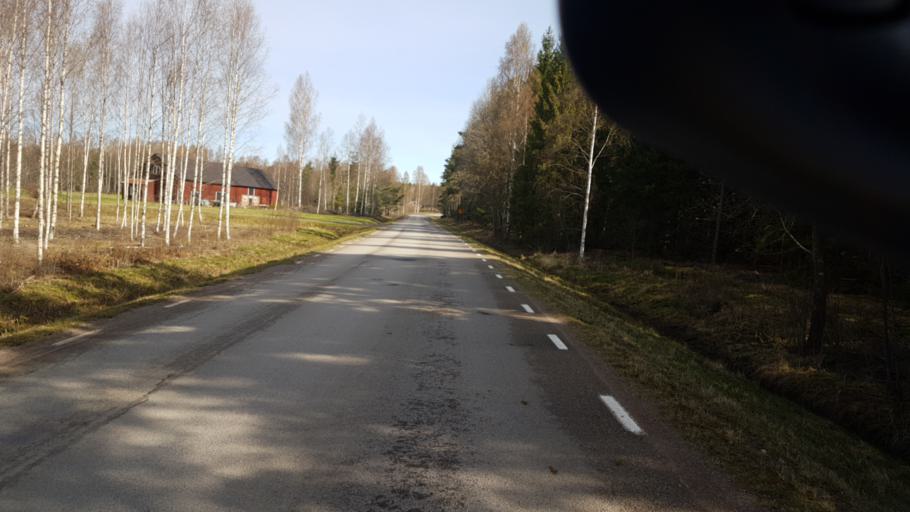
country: SE
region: Vaermland
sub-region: Arvika Kommun
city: Arvika
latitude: 59.5495
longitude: 12.7402
